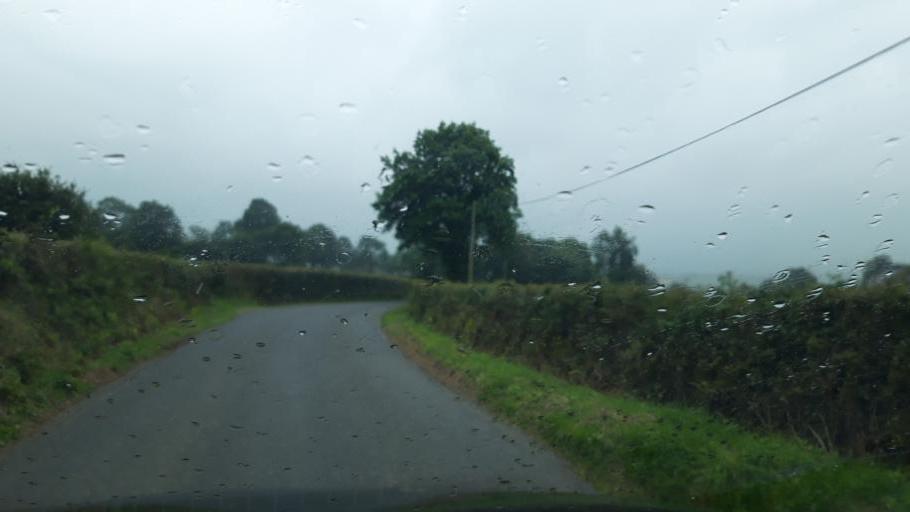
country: IE
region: Leinster
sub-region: Kilkenny
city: Ballyragget
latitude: 52.6856
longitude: -7.4306
